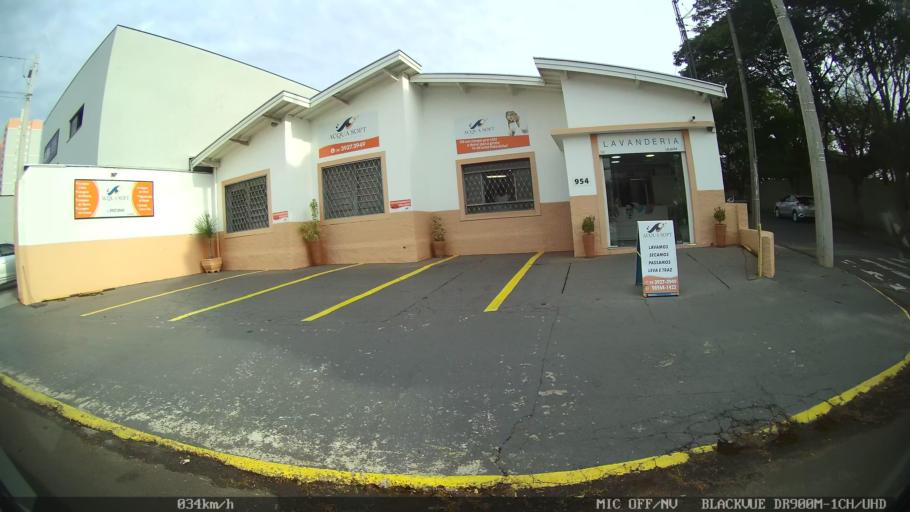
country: BR
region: Sao Paulo
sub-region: Piracicaba
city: Piracicaba
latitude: -22.7402
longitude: -47.6219
